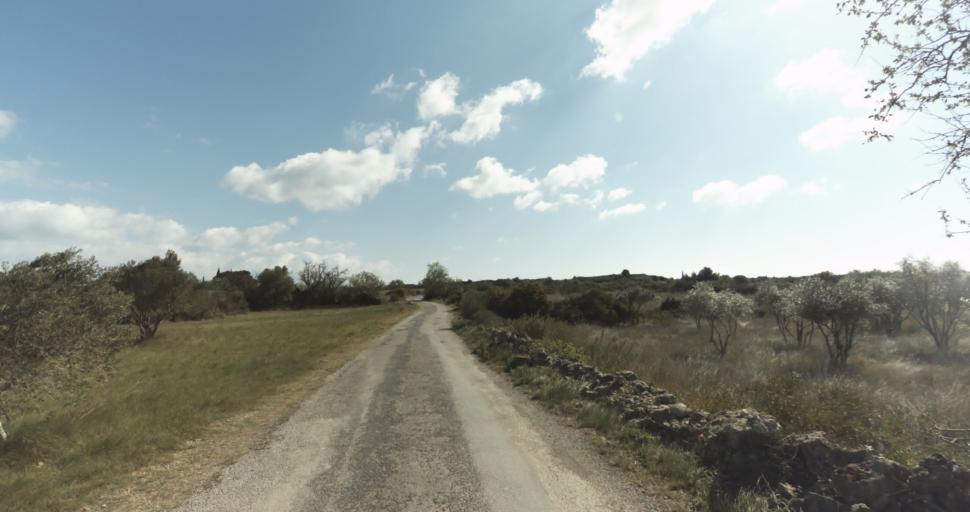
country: FR
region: Languedoc-Roussillon
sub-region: Departement de l'Aude
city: Leucate
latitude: 42.9164
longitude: 3.0321
